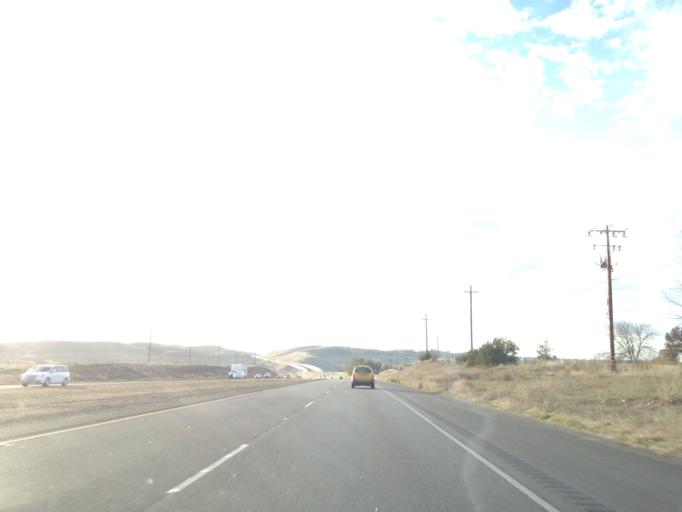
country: US
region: California
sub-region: San Luis Obispo County
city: Shandon
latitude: 35.6592
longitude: -120.4942
